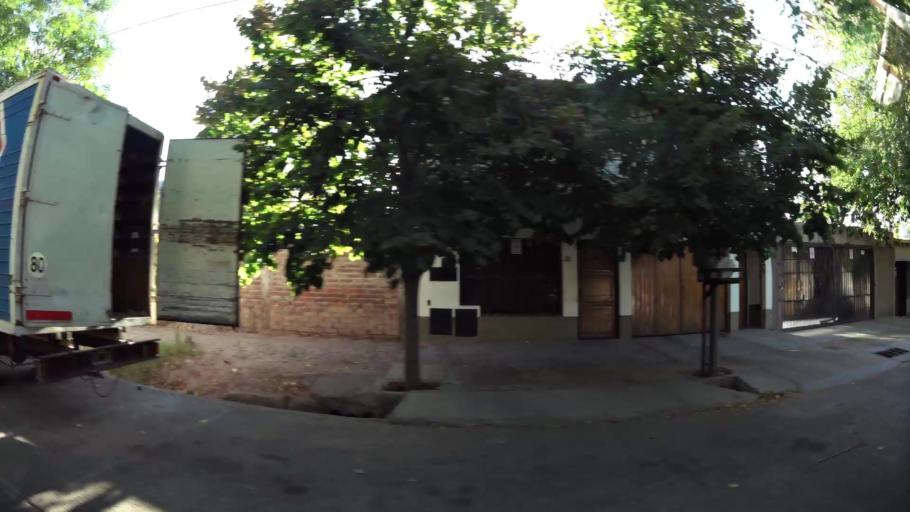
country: AR
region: Mendoza
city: Mendoza
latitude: -32.9061
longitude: -68.8414
